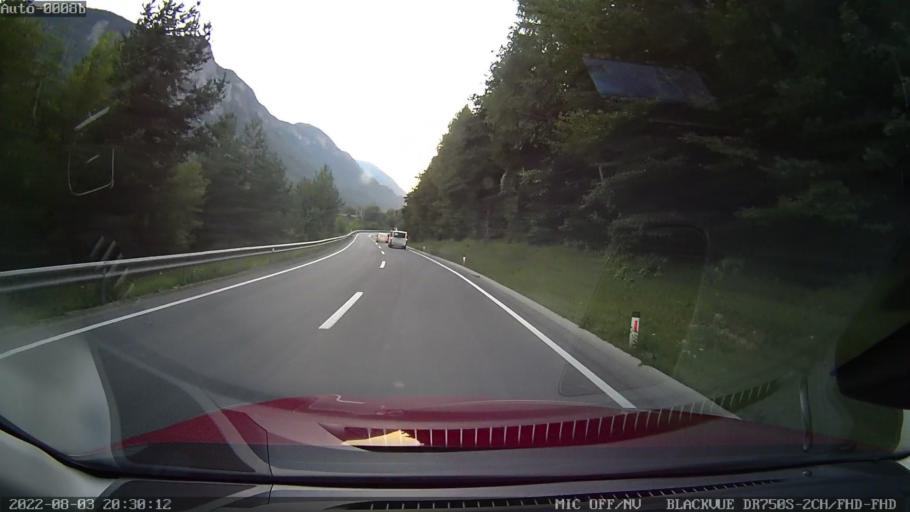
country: SI
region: Jesenice
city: Hrusica
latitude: 46.4445
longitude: 14.0298
